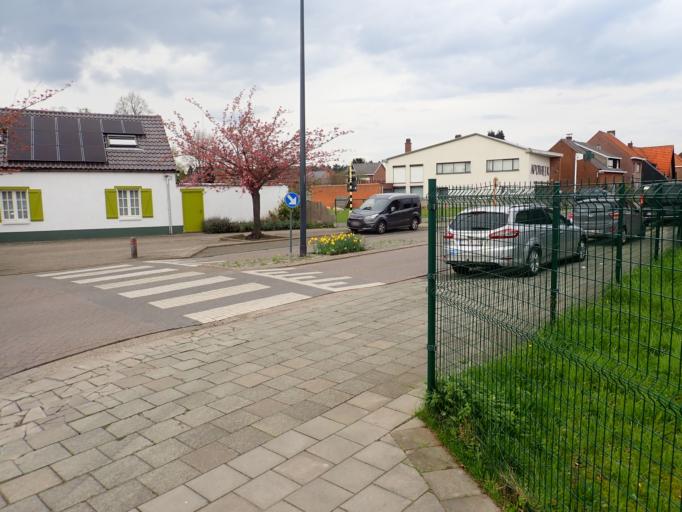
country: BE
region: Flanders
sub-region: Provincie Antwerpen
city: Vorselaar
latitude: 51.2028
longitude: 4.7656
